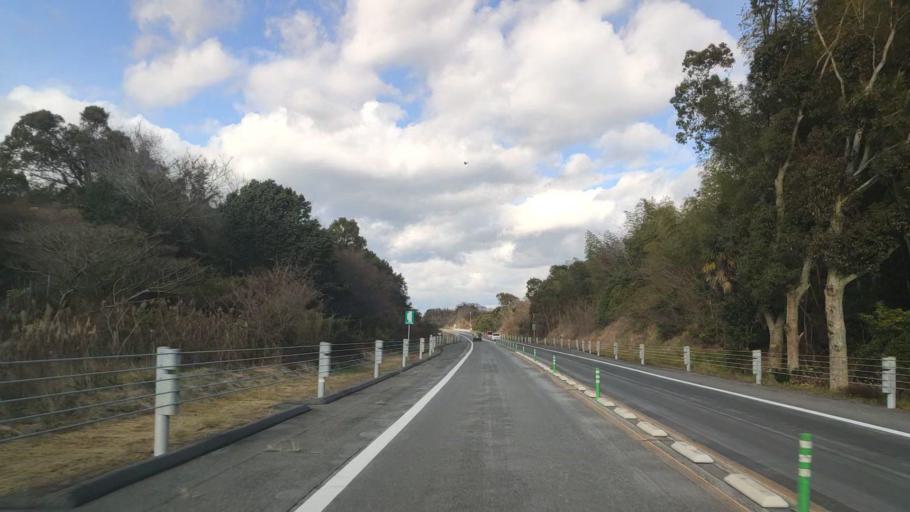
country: JP
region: Hiroshima
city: Innoshima
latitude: 34.2332
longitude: 133.0479
